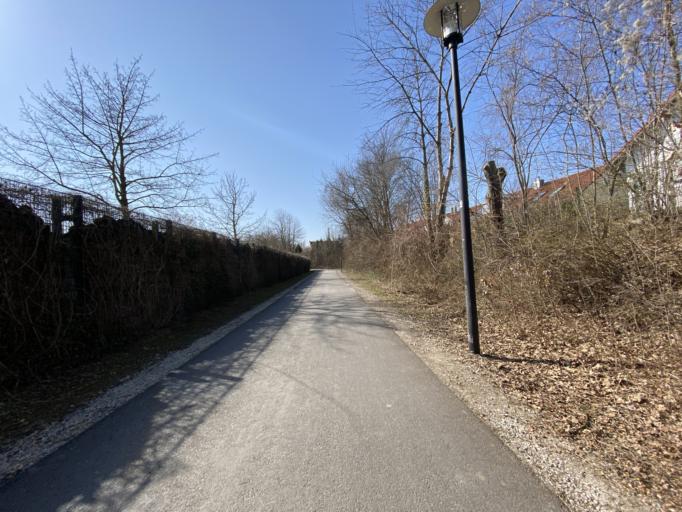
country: DE
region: Bavaria
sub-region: Upper Bavaria
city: Unterfoehring
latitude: 48.1890
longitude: 11.6454
